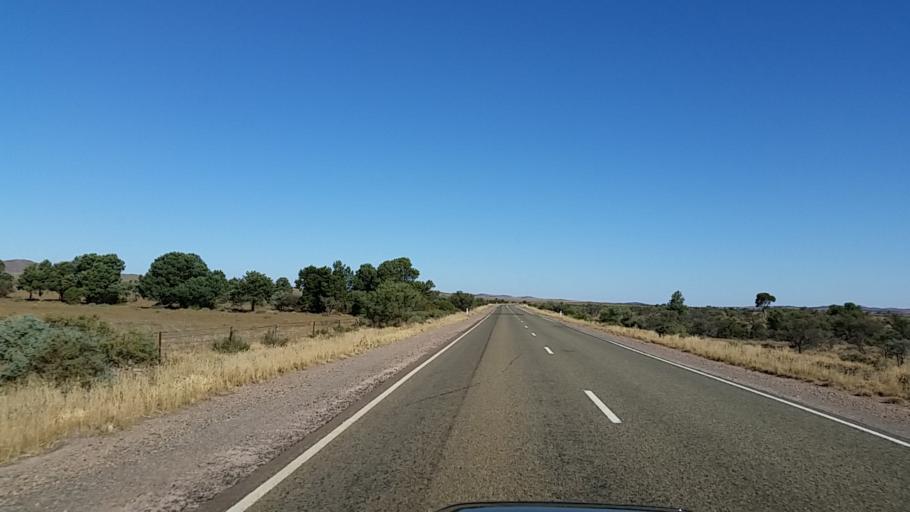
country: AU
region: South Australia
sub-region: Flinders Ranges
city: Quorn
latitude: -32.4345
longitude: 138.5336
